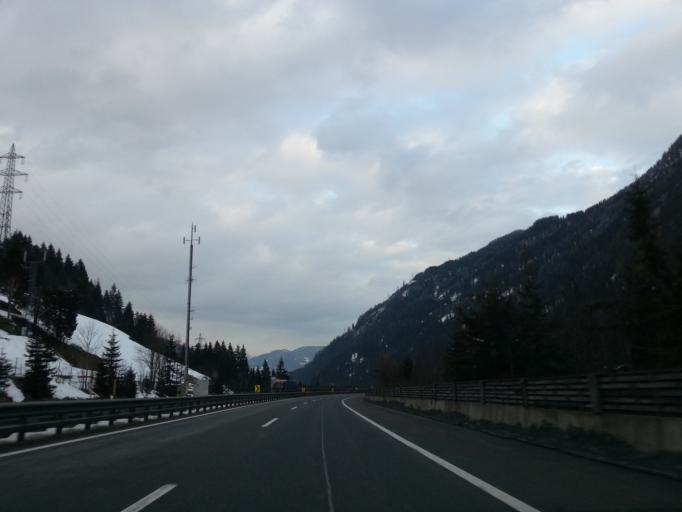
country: AT
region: Salzburg
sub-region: Politischer Bezirk Sankt Johann im Pongau
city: Flachau
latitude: 47.3067
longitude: 13.3930
